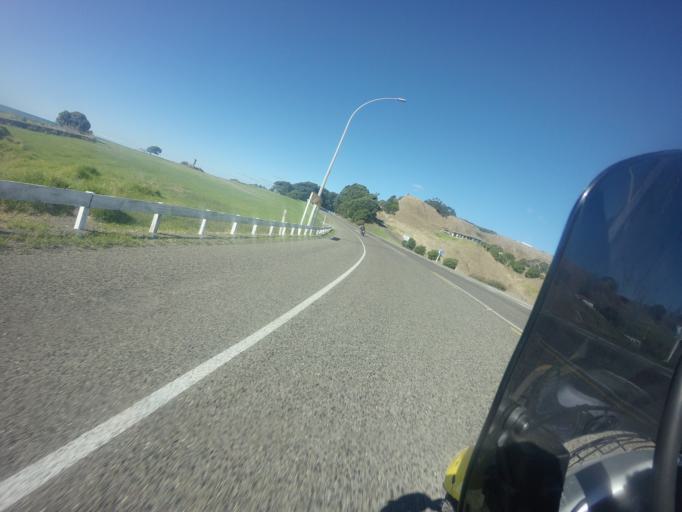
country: NZ
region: Bay of Plenty
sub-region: Opotiki District
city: Opotiki
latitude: -37.9921
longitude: 177.2176
